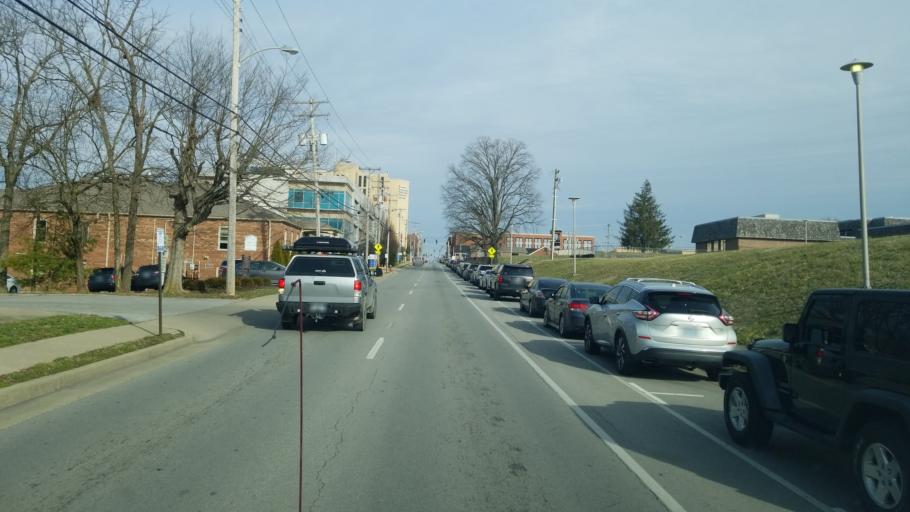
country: US
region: Kentucky
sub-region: Boyle County
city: Danville
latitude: 37.6419
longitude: -84.7729
